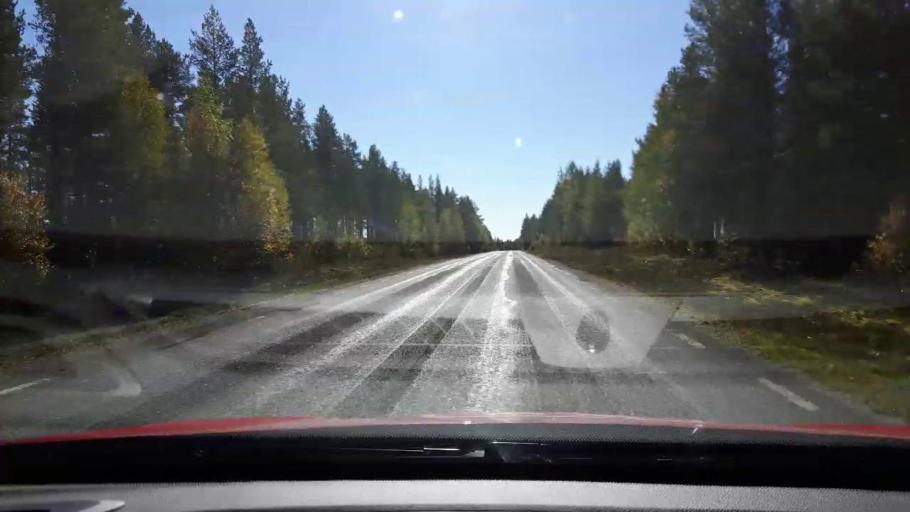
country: SE
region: Jaemtland
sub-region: Harjedalens Kommun
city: Sveg
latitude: 62.3452
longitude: 14.0352
